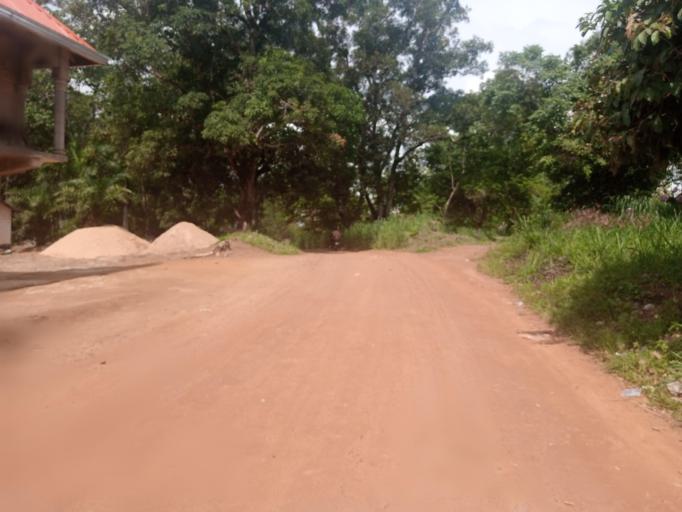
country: SL
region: Southern Province
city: Bo
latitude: 7.9686
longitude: -11.7480
